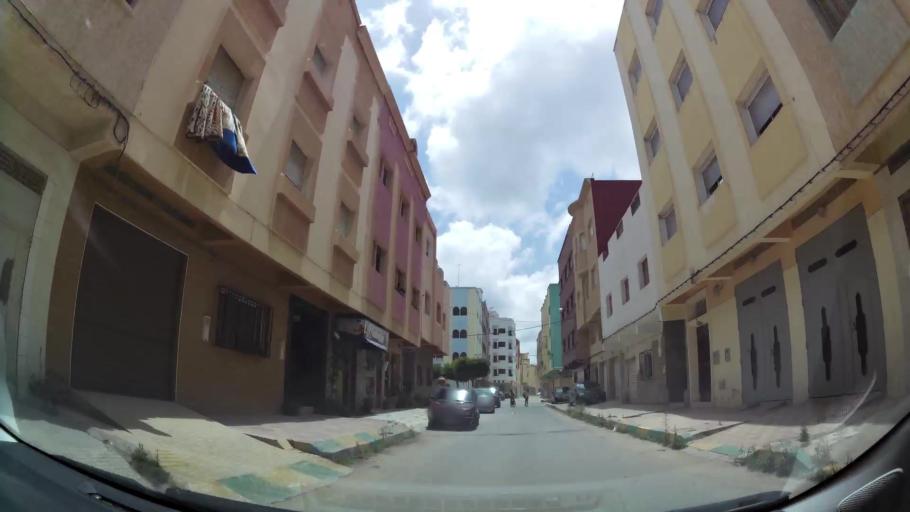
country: MA
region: Oriental
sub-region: Nador
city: Nador
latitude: 35.1692
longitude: -2.9206
